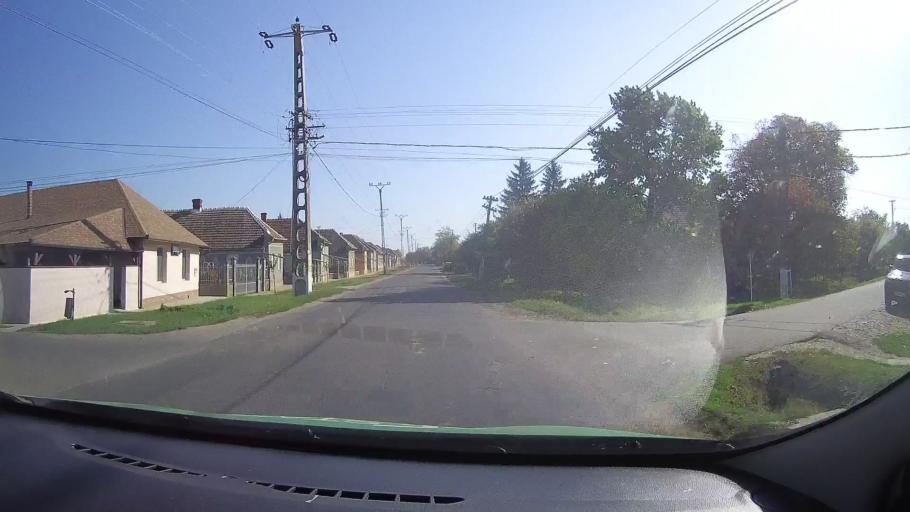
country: RO
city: Foieni
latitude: 47.6958
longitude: 22.3938
